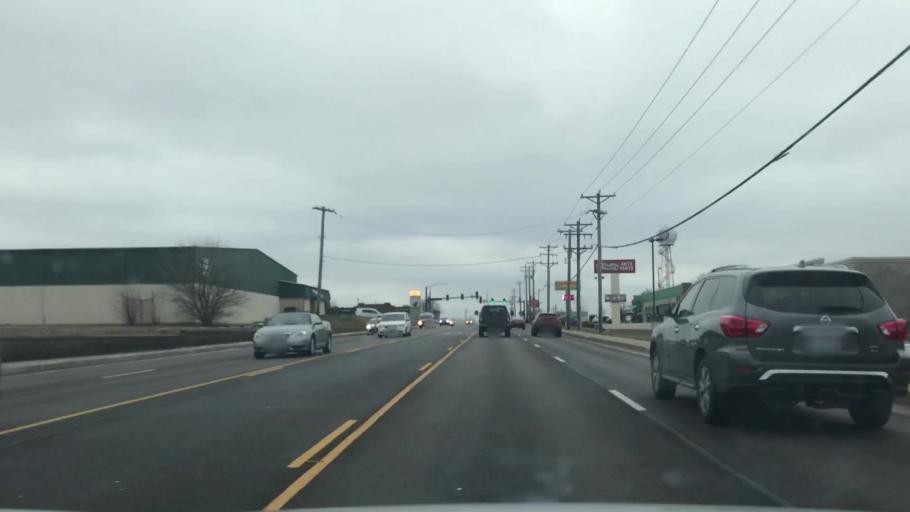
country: US
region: Missouri
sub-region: Saint Charles County
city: Saint Peters
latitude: 38.7911
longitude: -90.5697
